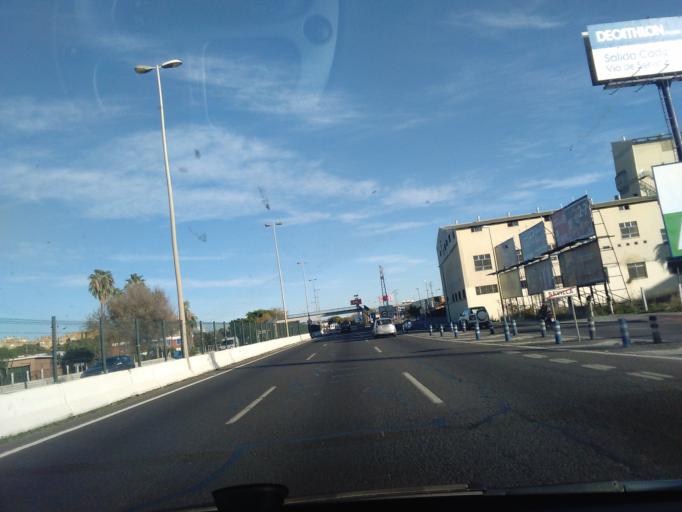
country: ES
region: Andalusia
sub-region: Provincia de Sevilla
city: Sevilla
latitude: 37.3859
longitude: -5.9284
